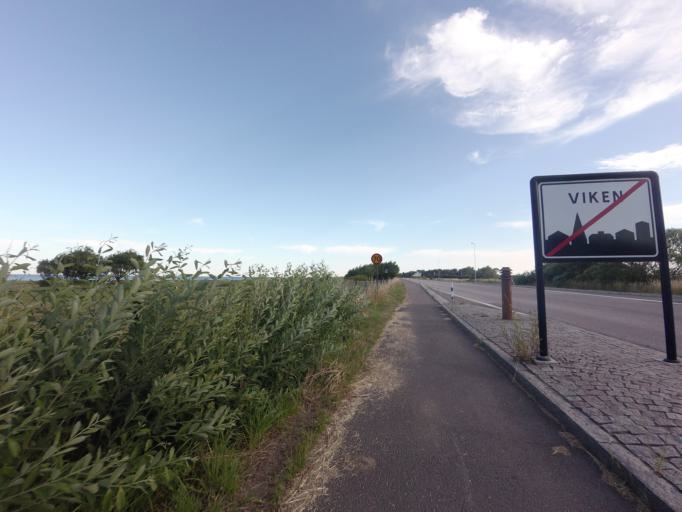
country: SE
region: Skane
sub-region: Hoganas Kommun
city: Hoganas
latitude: 56.1636
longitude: 12.5671
